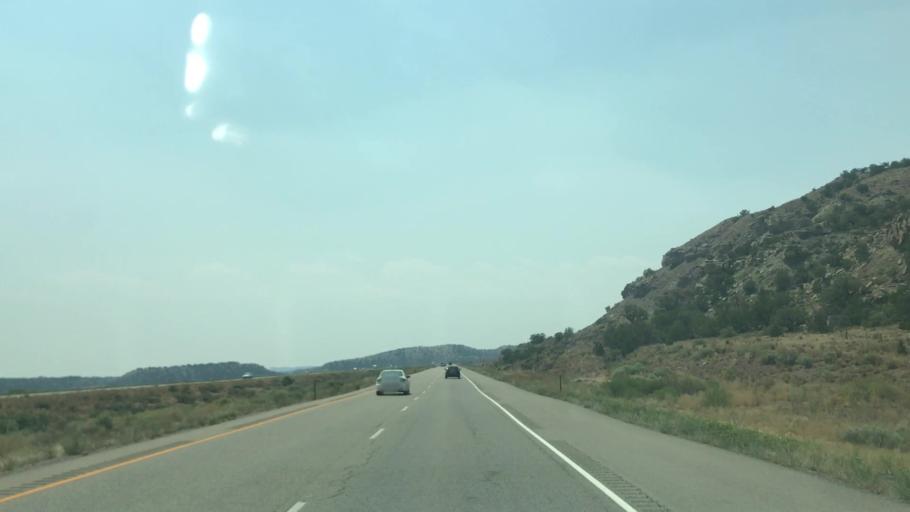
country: US
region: Colorado
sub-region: Garfield County
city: Parachute
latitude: 39.3885
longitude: -108.1385
